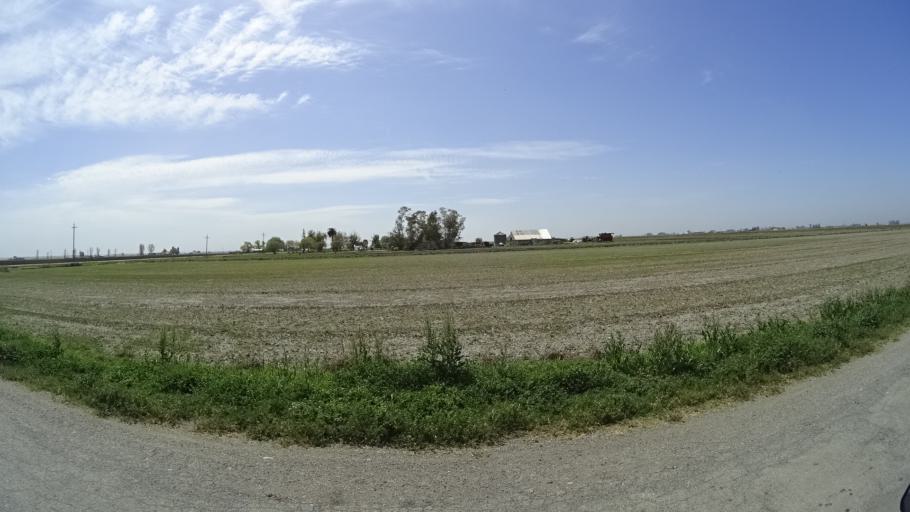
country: US
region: California
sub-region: Glenn County
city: Willows
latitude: 39.5733
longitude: -122.0664
